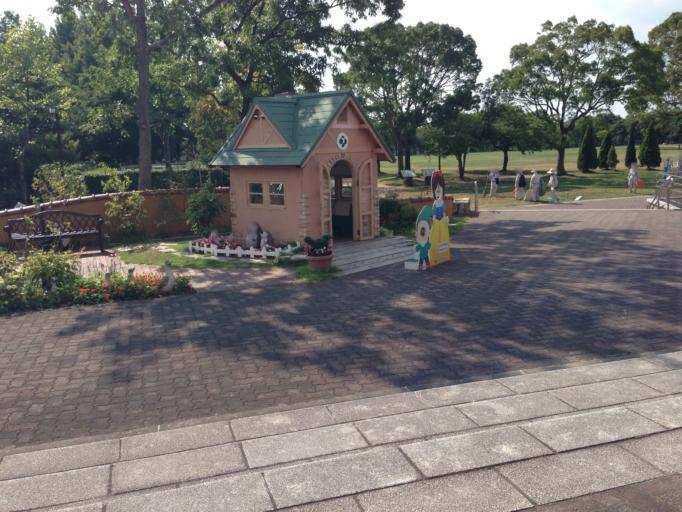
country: JP
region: Hyogo
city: Kobe
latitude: 34.7078
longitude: 135.1149
